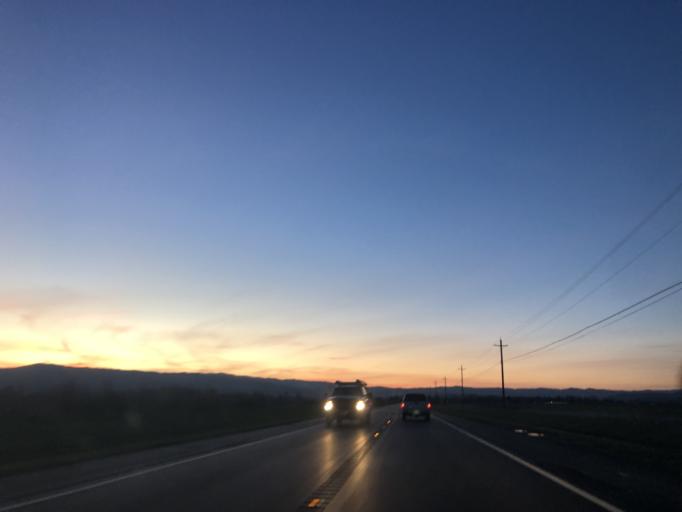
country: US
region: California
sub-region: Yolo County
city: Esparto
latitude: 38.6852
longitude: -121.9906
